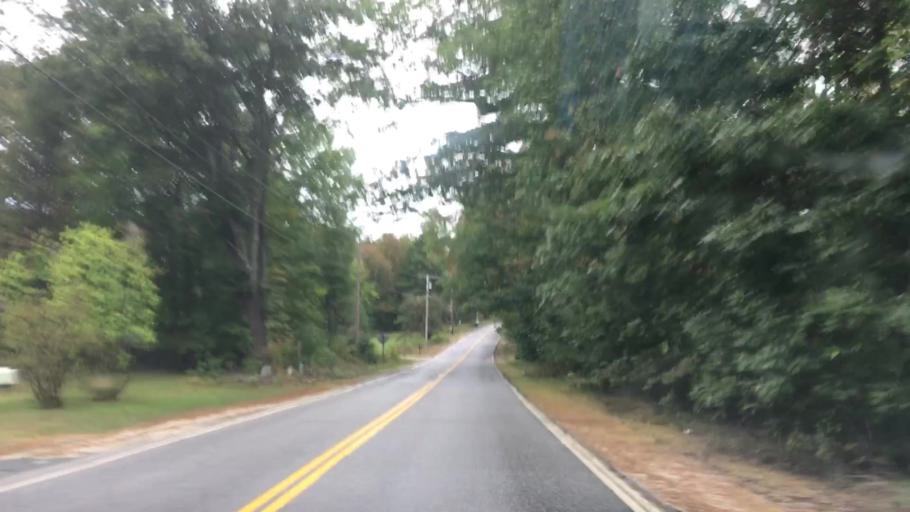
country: US
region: Maine
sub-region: Cumberland County
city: Raymond
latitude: 43.9650
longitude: -70.4658
